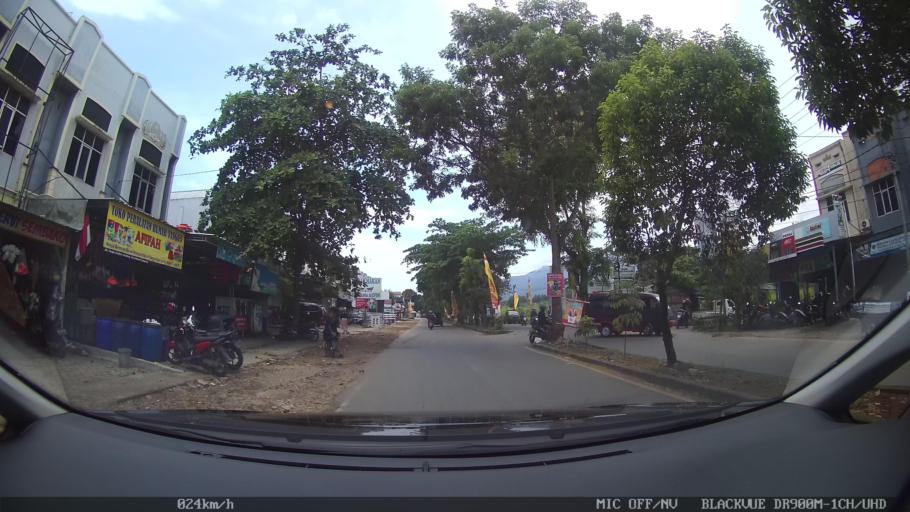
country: ID
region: Lampung
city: Kedaton
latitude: -5.3986
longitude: 105.2036
